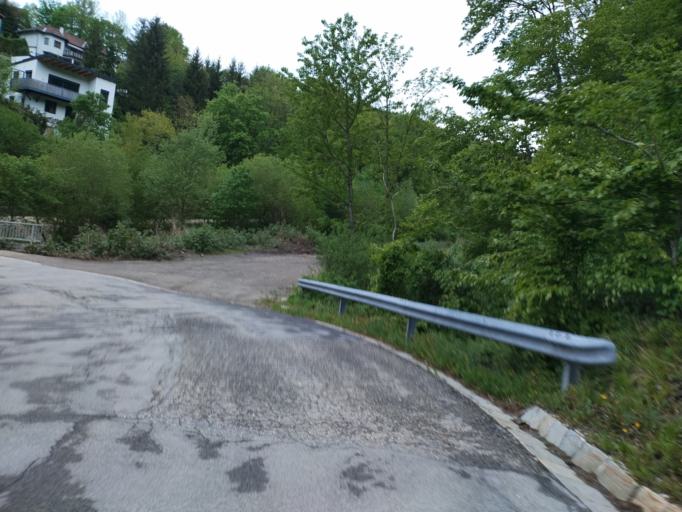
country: AT
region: Lower Austria
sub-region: Politischer Bezirk Wien-Umgebung
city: Mauerbach
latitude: 48.2465
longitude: 16.2199
